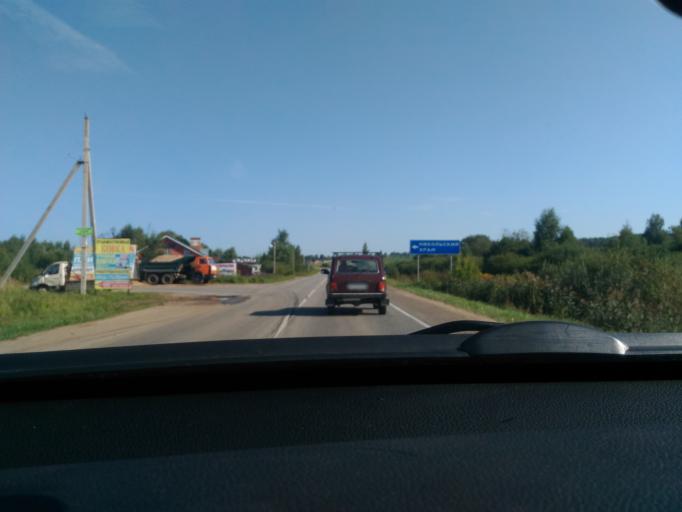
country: RU
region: Moskovskaya
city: Podosinki
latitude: 56.2272
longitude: 37.5485
